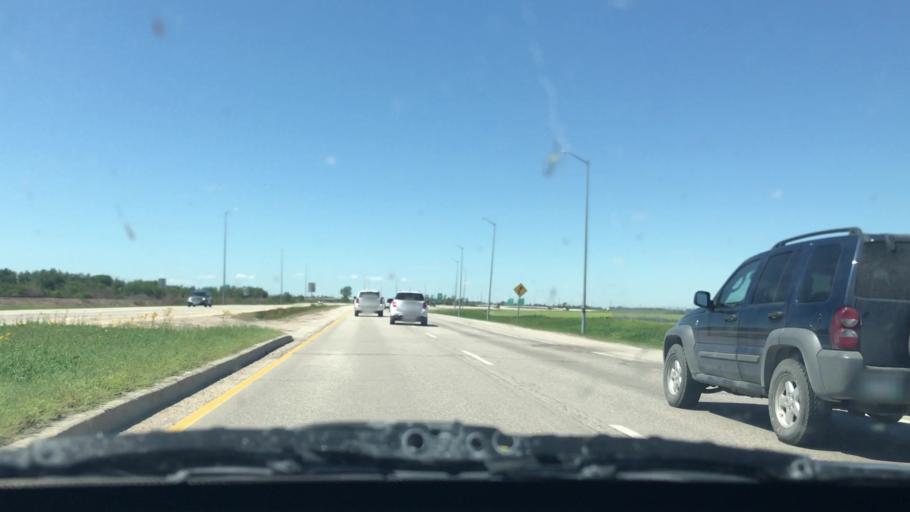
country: CA
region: Manitoba
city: Winnipeg
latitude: 49.8215
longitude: -96.9390
